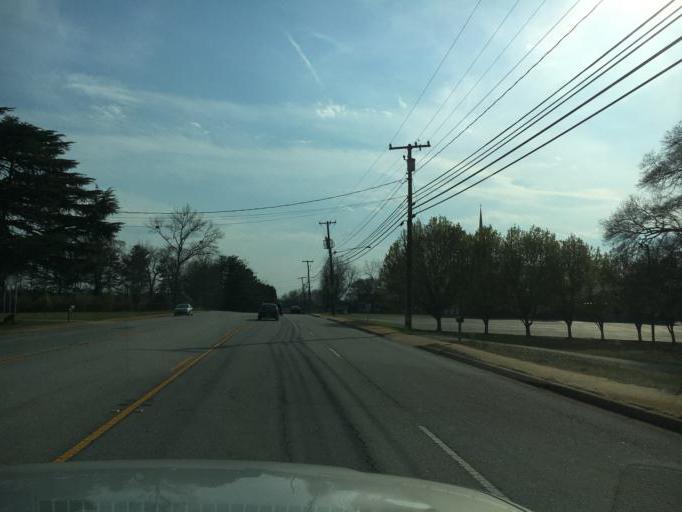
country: US
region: South Carolina
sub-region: Spartanburg County
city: Spartanburg
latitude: 34.9966
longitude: -81.9124
